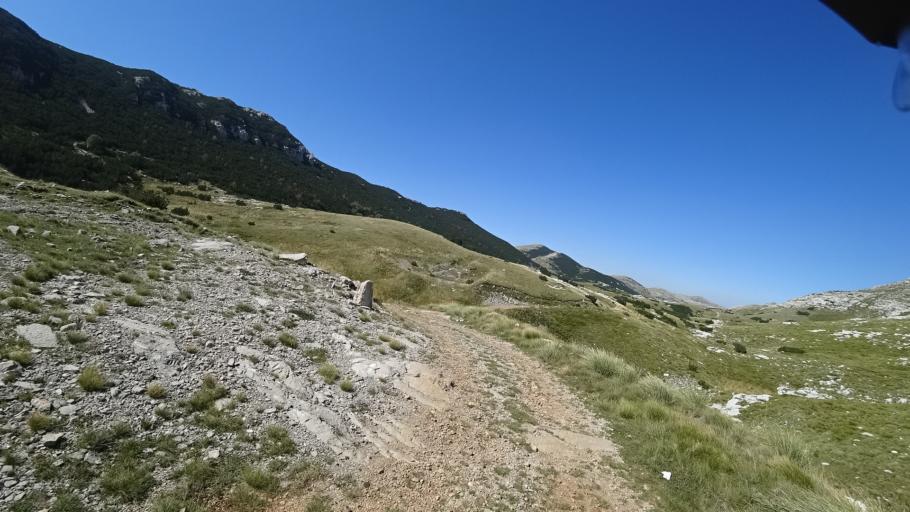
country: HR
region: Splitsko-Dalmatinska
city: Hrvace
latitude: 43.9373
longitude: 16.5926
